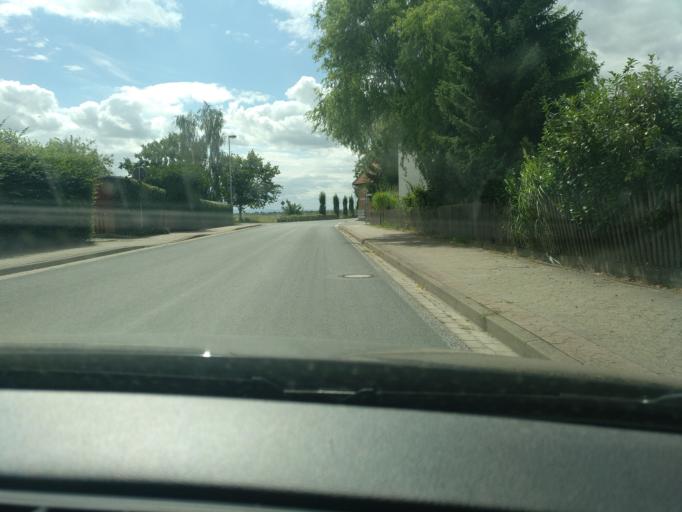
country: DE
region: Lower Saxony
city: Sickte
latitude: 52.2125
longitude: 10.6377
